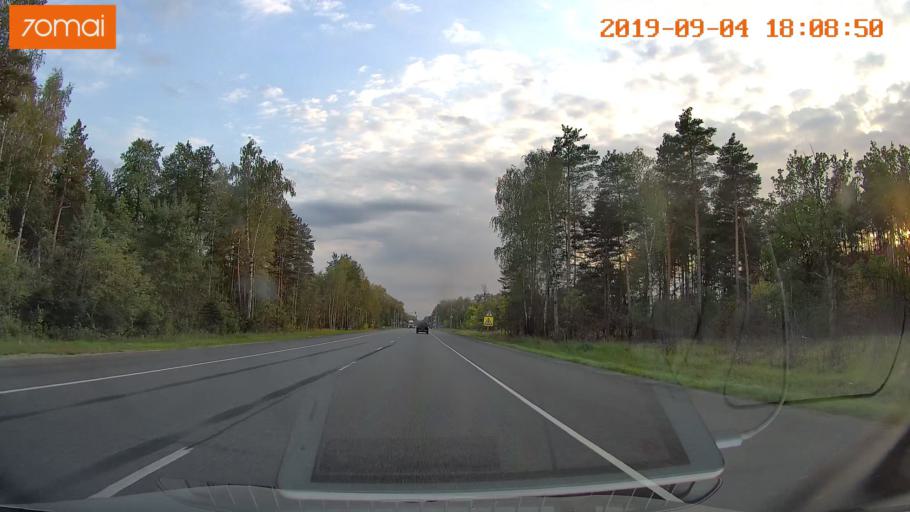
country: RU
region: Moskovskaya
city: Khorlovo
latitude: 55.4012
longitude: 38.7806
